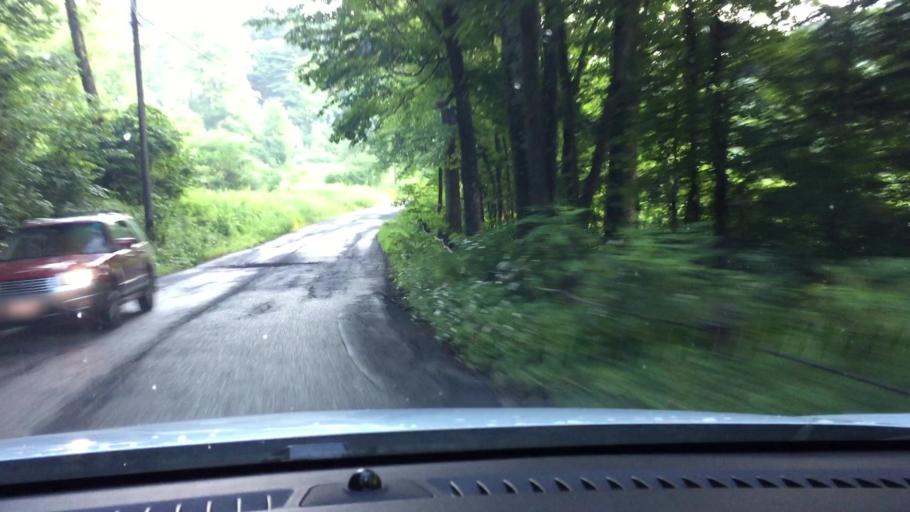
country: US
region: Massachusetts
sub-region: Hampshire County
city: Chesterfield
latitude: 42.3268
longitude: -72.9327
